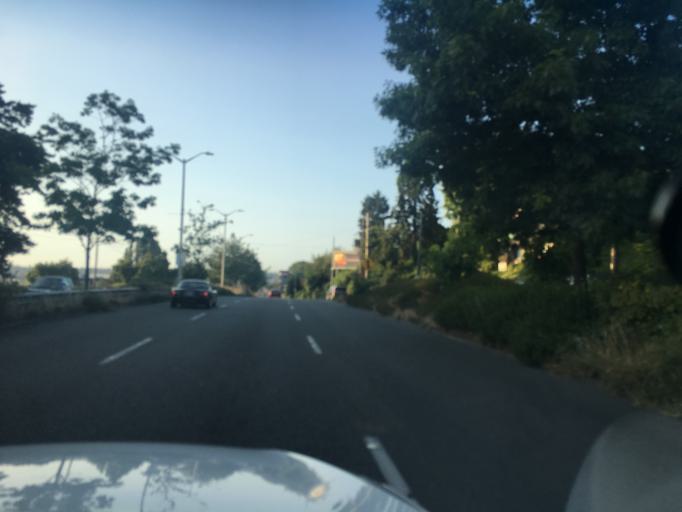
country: US
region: Washington
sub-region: King County
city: Seattle
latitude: 47.6495
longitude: -122.3763
